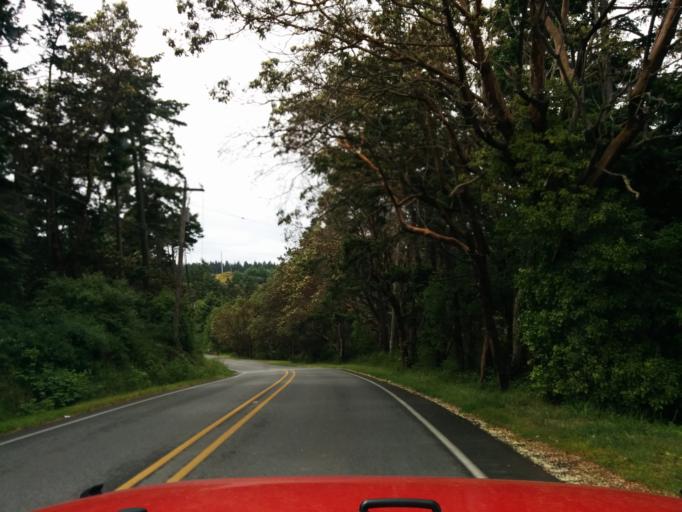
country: US
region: Washington
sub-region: Island County
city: Coupeville
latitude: 48.2144
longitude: -122.7165
